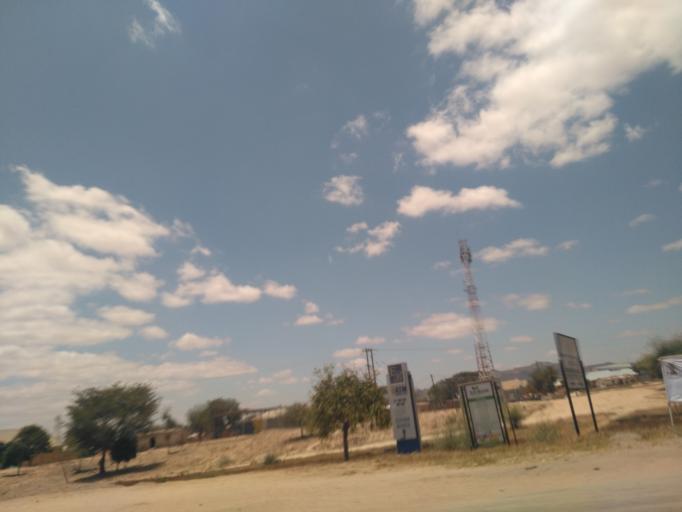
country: TZ
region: Dodoma
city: Dodoma
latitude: -6.1751
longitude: 35.7638
